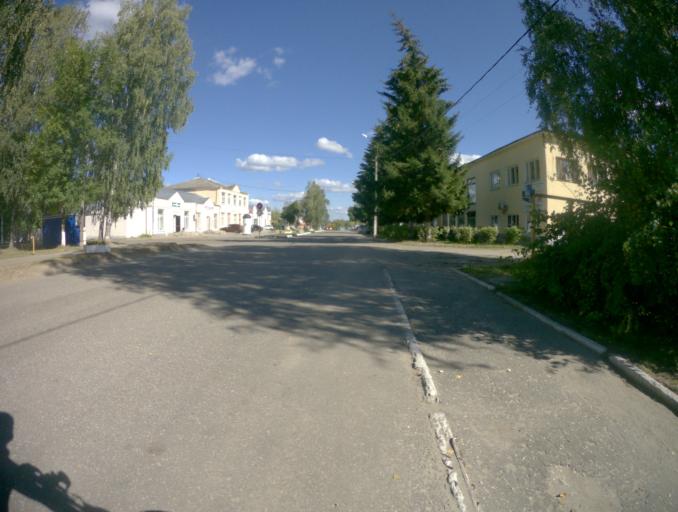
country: RU
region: Vladimir
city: Krasnaya Gorbatka
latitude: 55.8649
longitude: 41.7632
